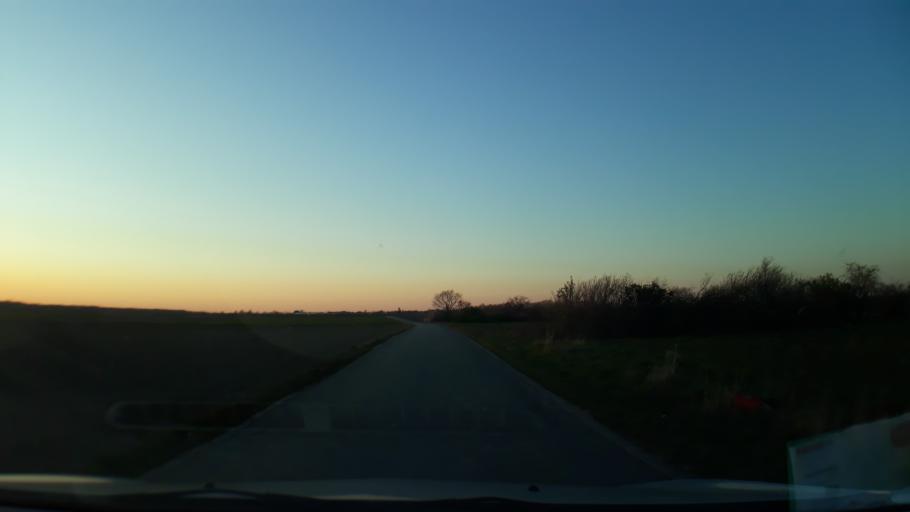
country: DE
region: North Rhine-Westphalia
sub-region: Regierungsbezirk Koln
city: Vettweiss
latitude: 50.7243
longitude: 6.6066
